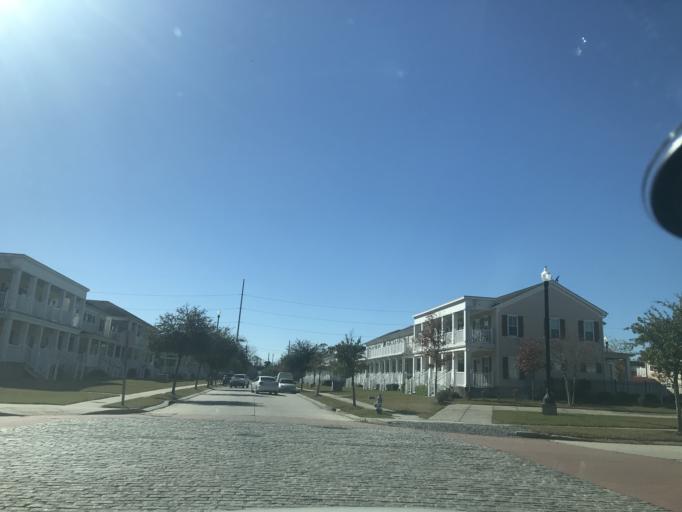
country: US
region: Louisiana
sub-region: Orleans Parish
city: New Orleans
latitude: 29.9520
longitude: -90.0937
